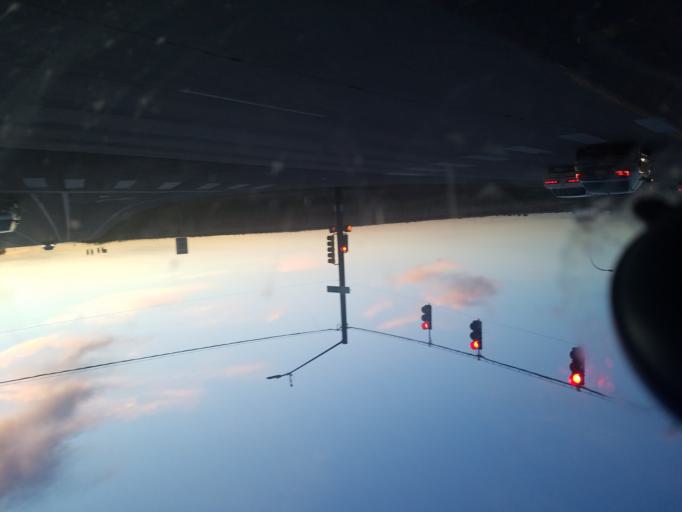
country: US
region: Colorado
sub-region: El Paso County
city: Cimarron Hills
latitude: 38.8248
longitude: -104.7247
